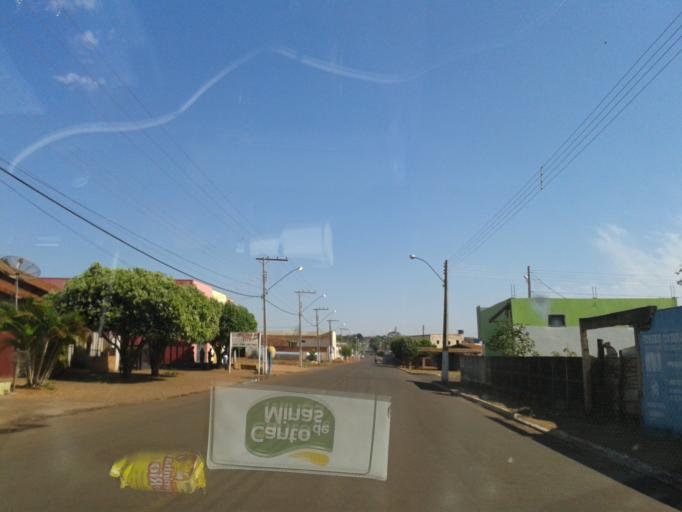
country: BR
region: Minas Gerais
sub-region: Santa Vitoria
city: Santa Vitoria
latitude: -19.0075
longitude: -50.5463
